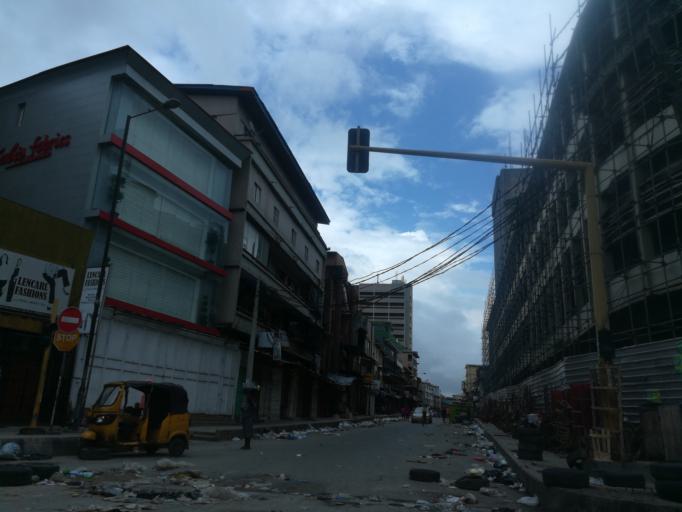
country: NG
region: Lagos
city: Lagos
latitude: 6.4557
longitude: 3.3838
